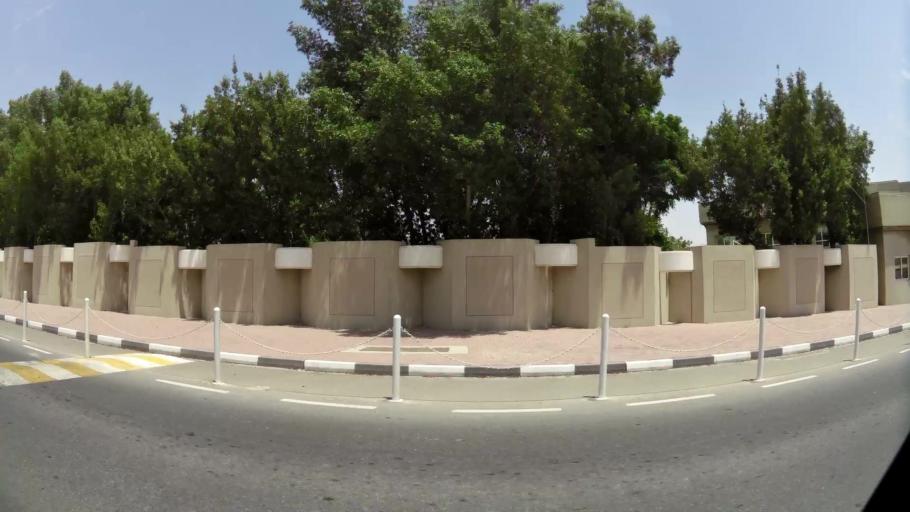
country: AE
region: Dubai
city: Dubai
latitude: 25.1579
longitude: 55.2144
